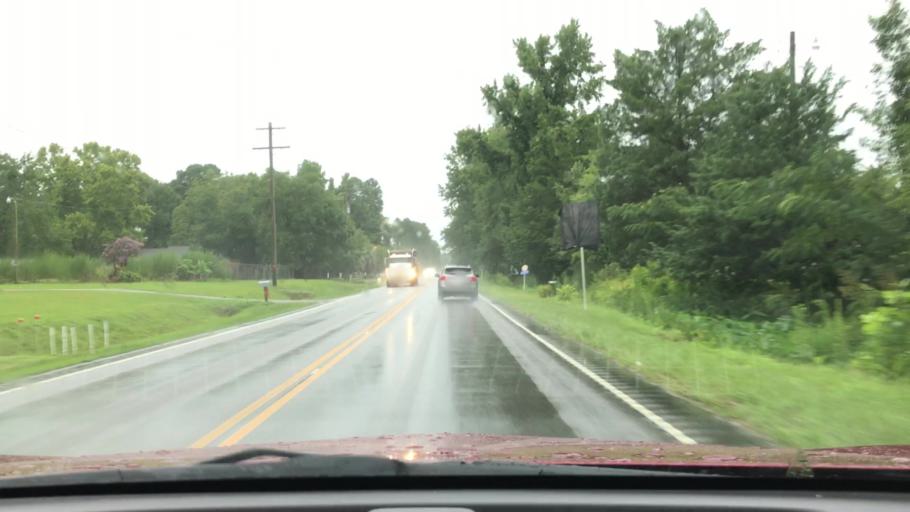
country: US
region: South Carolina
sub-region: Horry County
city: Conway
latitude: 33.8092
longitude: -79.0779
